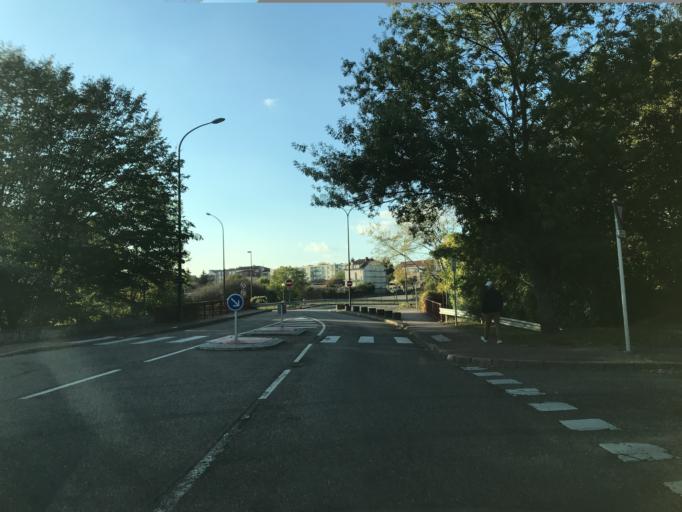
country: FR
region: Lorraine
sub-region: Departement de la Moselle
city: Saint-Julien-les-Metz
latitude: 49.1180
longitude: 6.2127
